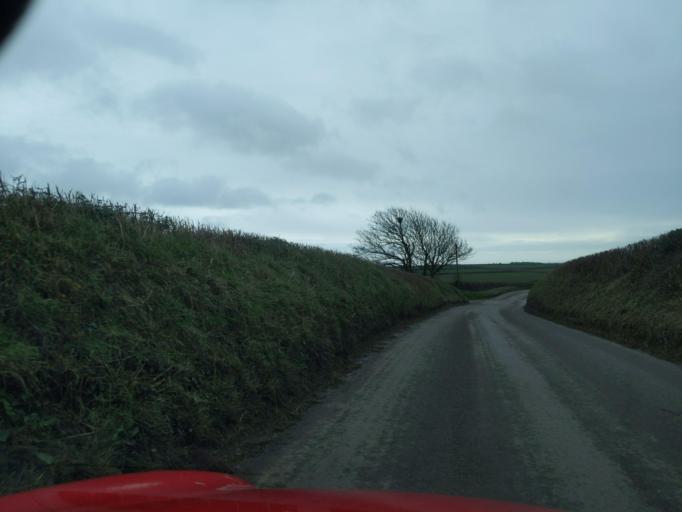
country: GB
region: England
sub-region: Devon
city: Modbury
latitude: 50.3235
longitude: -3.8856
